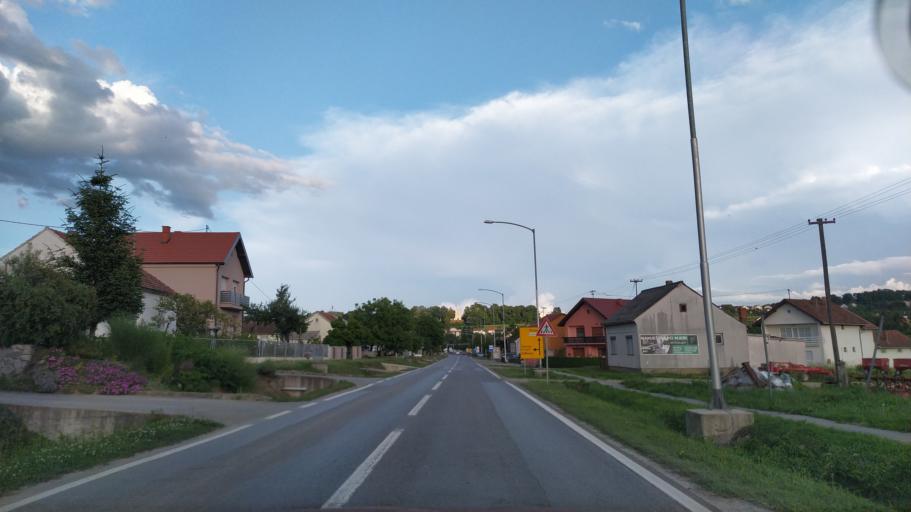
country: HR
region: Osjecko-Baranjska
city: Martin
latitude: 45.4899
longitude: 18.0707
